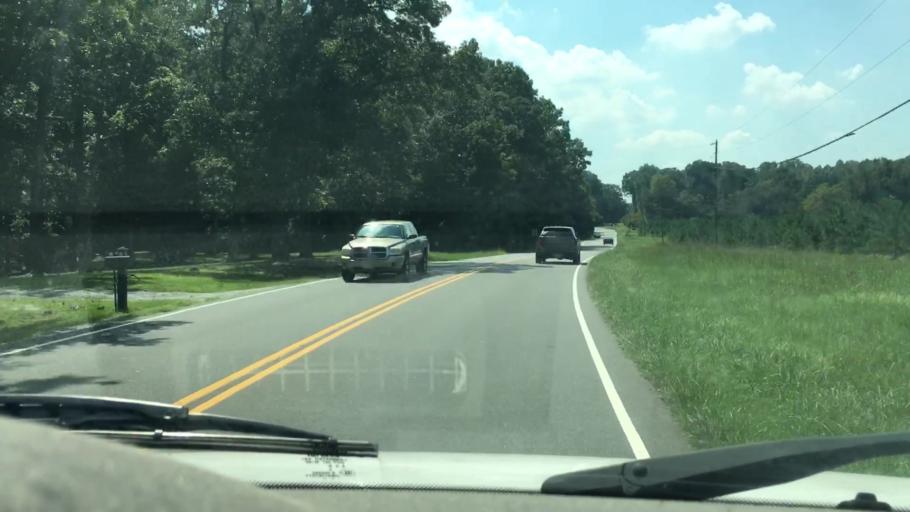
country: US
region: North Carolina
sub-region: Mecklenburg County
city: Huntersville
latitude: 35.3717
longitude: -80.8549
